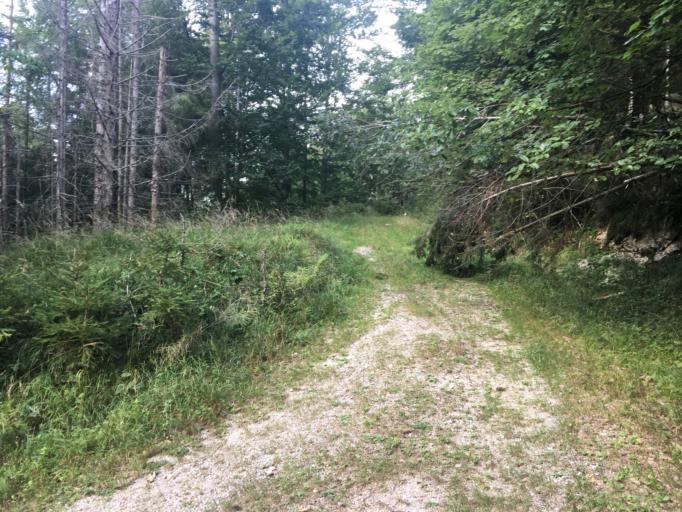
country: AT
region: Salzburg
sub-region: Politischer Bezirk Salzburg-Umgebung
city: Sankt Gilgen
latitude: 47.7825
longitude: 13.4044
